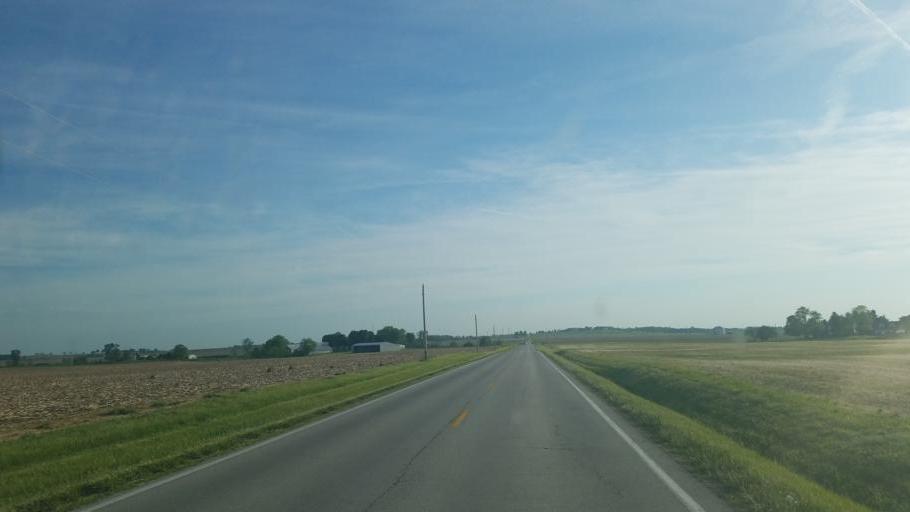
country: US
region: Ohio
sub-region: Highland County
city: Greenfield
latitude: 39.3876
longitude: -83.3315
